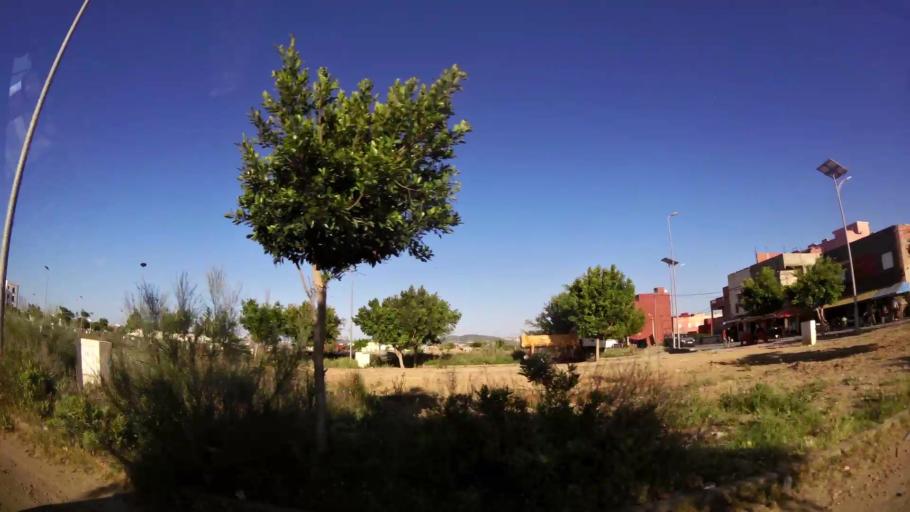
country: MA
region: Oriental
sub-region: Berkane-Taourirt
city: Madagh
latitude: 35.0837
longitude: -2.2544
